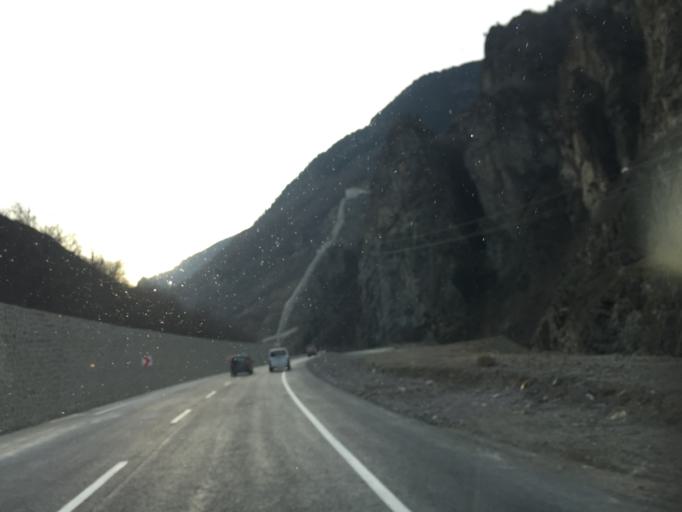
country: TR
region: Trabzon
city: Macka
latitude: 40.7372
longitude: 39.5443
